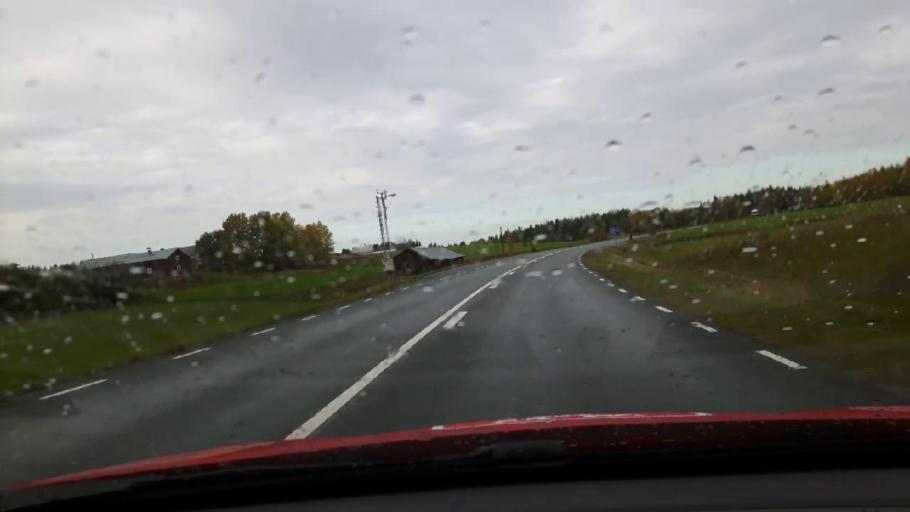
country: SE
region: Jaemtland
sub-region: Krokoms Kommun
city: Krokom
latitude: 63.0757
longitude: 14.2938
